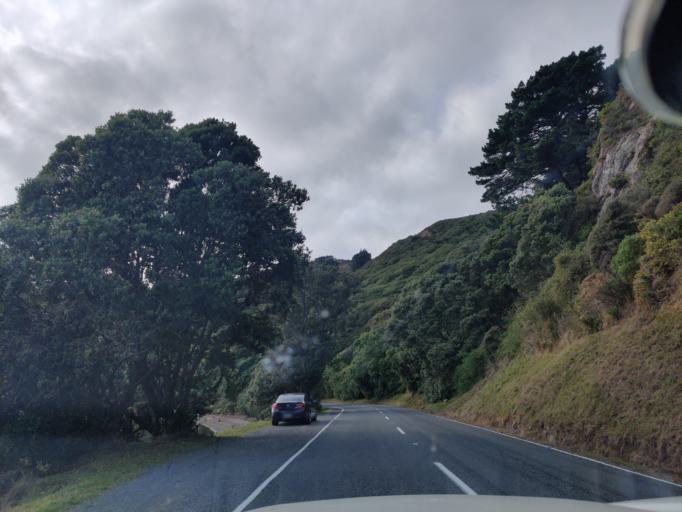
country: NZ
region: Wellington
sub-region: Wellington City
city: Wellington
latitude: -41.2991
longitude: 174.8184
